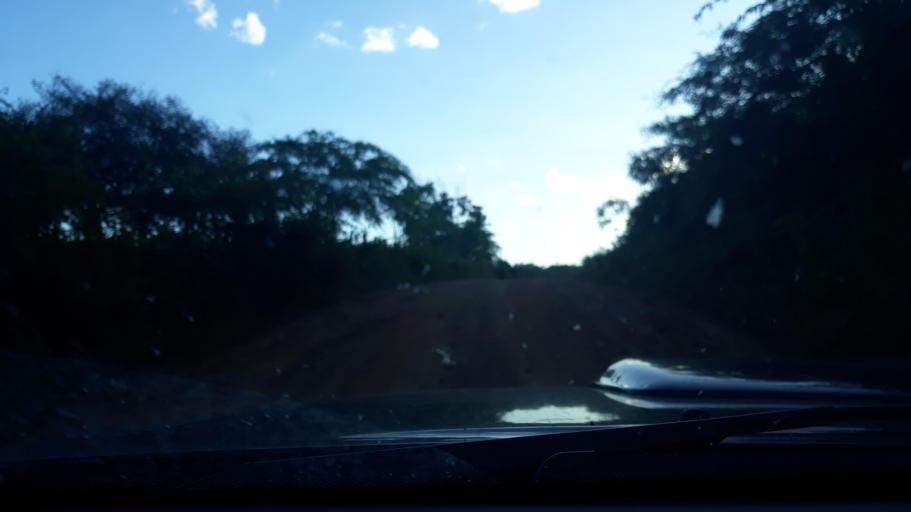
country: BR
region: Bahia
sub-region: Riacho De Santana
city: Riacho de Santana
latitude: -13.8137
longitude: -42.7218
